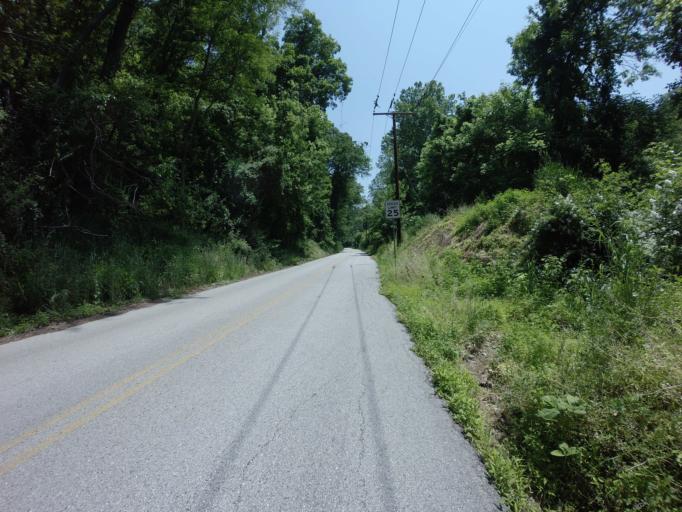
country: US
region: Maryland
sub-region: Howard County
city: Ilchester
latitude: 39.2570
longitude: -76.7779
